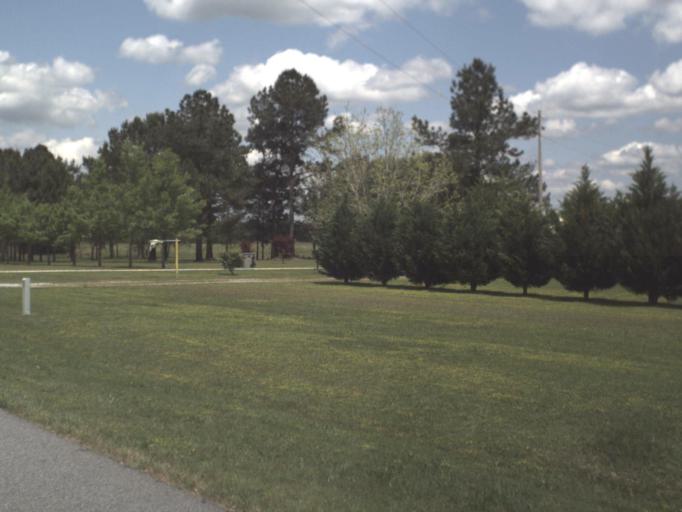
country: US
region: Florida
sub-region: Escambia County
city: Molino
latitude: 30.8413
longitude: -87.4351
